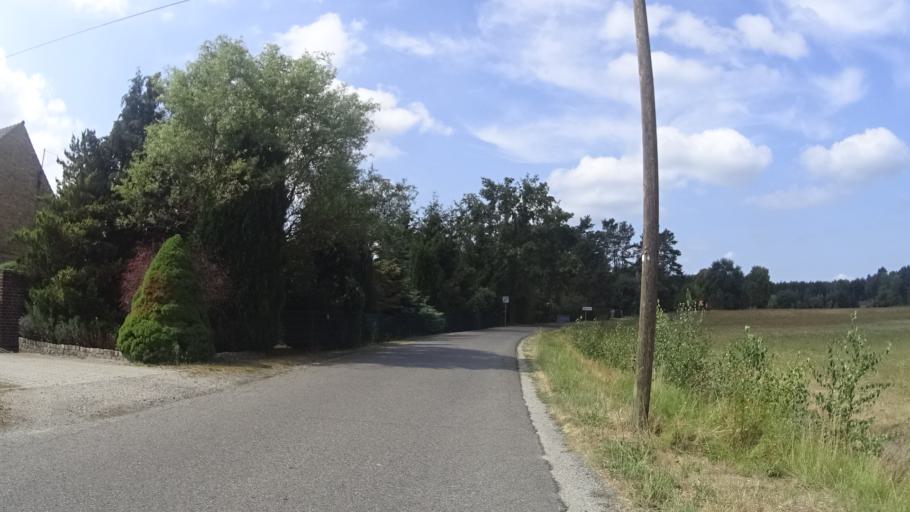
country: DE
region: Brandenburg
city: Tschernitz
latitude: 51.5827
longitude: 14.6091
